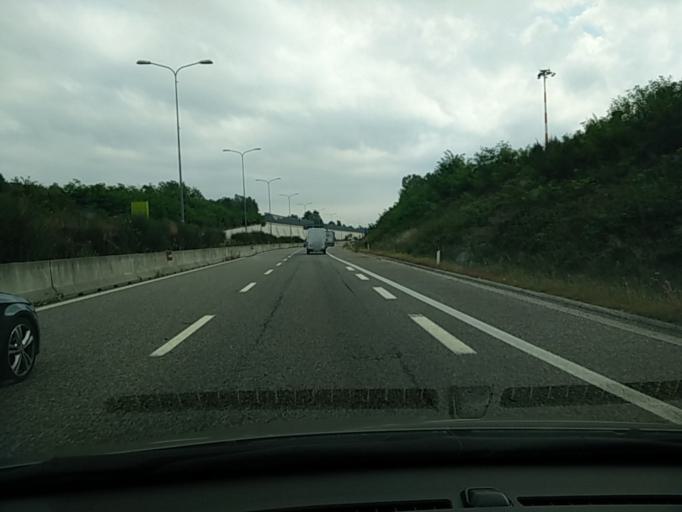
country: IT
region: Lombardy
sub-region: Provincia di Varese
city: Vizzola Ticino
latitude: 45.6194
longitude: 8.7075
